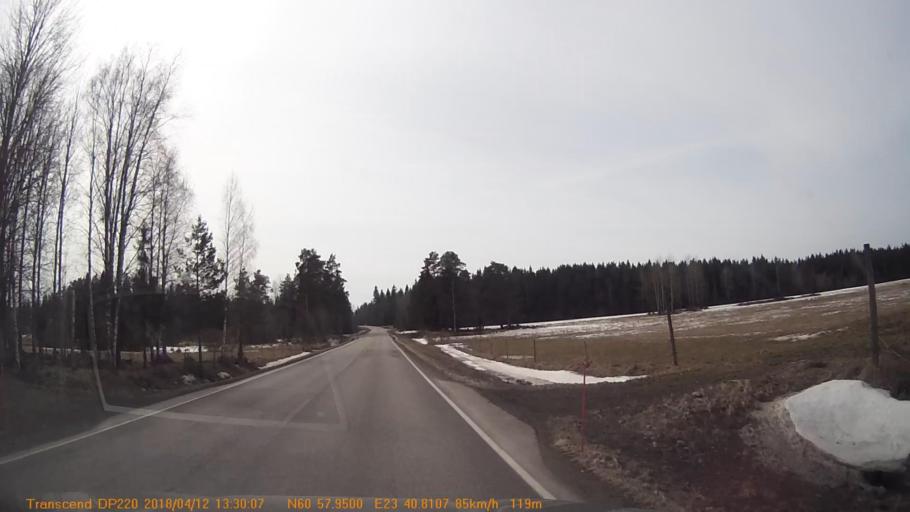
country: FI
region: Haeme
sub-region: Forssa
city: Forssa
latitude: 60.9660
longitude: 23.6806
